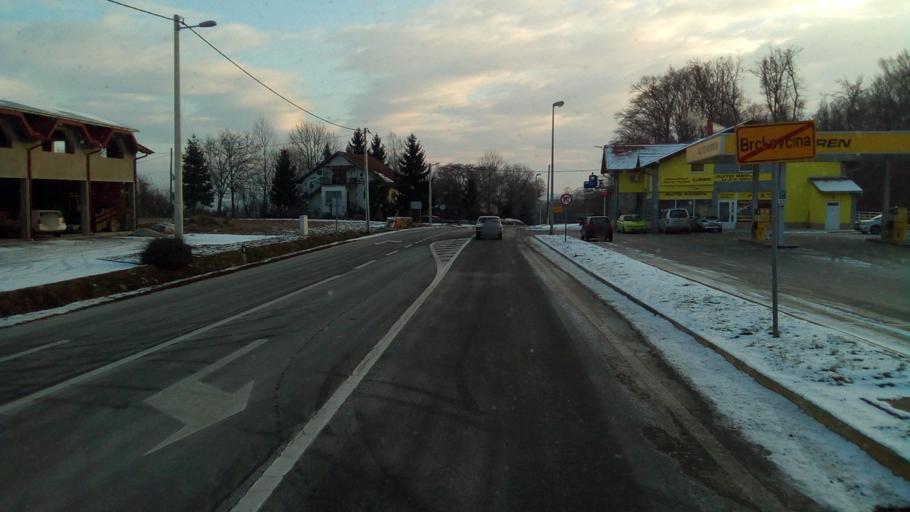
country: HR
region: Koprivnicko-Krizevacka
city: Krizevci
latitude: 46.0138
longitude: 16.5176
